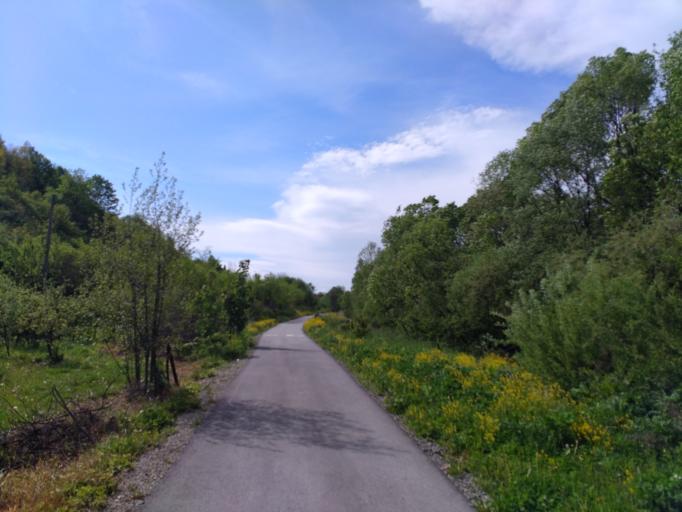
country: PL
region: Lesser Poland Voivodeship
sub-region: Powiat nowosadecki
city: Lacko
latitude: 49.5708
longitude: 20.4267
